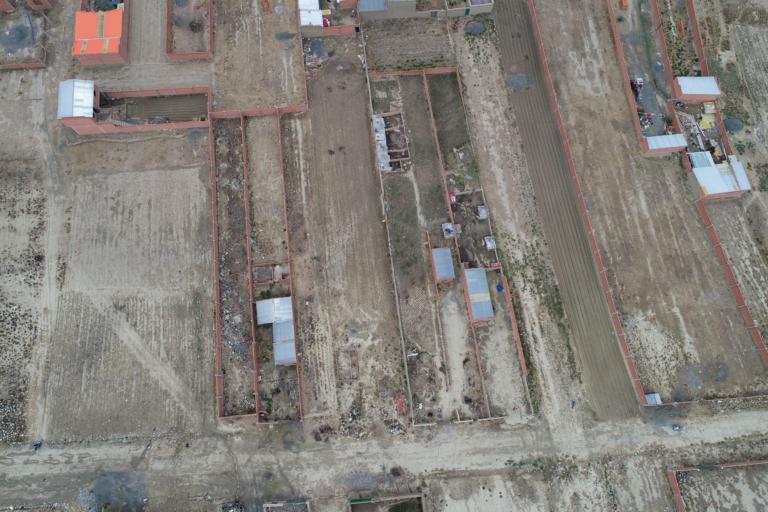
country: BO
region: La Paz
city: Achacachi
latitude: -16.0529
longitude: -68.6855
